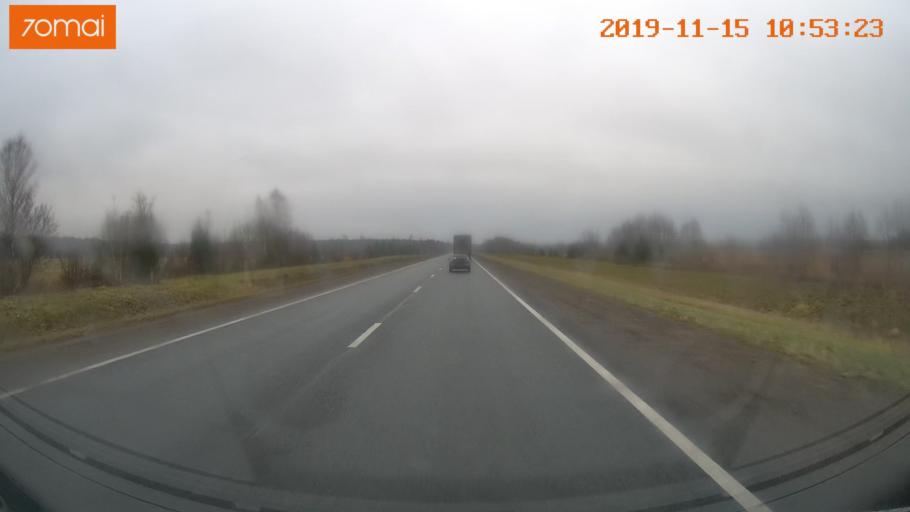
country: RU
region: Vologda
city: Chebsara
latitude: 59.1695
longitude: 38.7529
